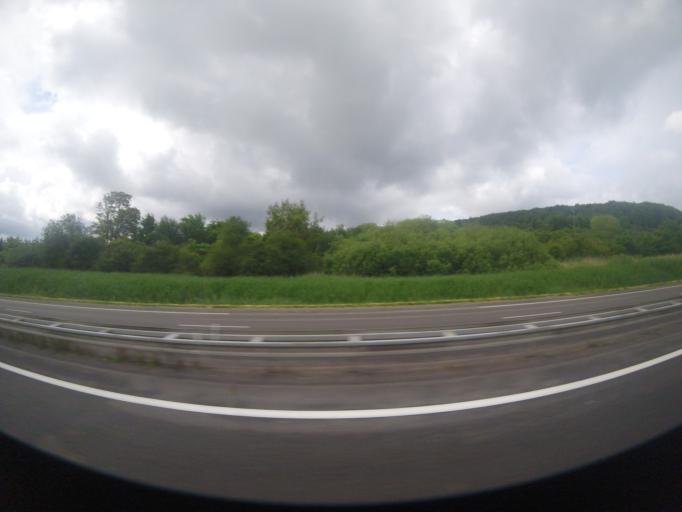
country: FR
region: Lorraine
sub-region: Departement de la Meuse
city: Etain
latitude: 49.1130
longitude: 5.5574
